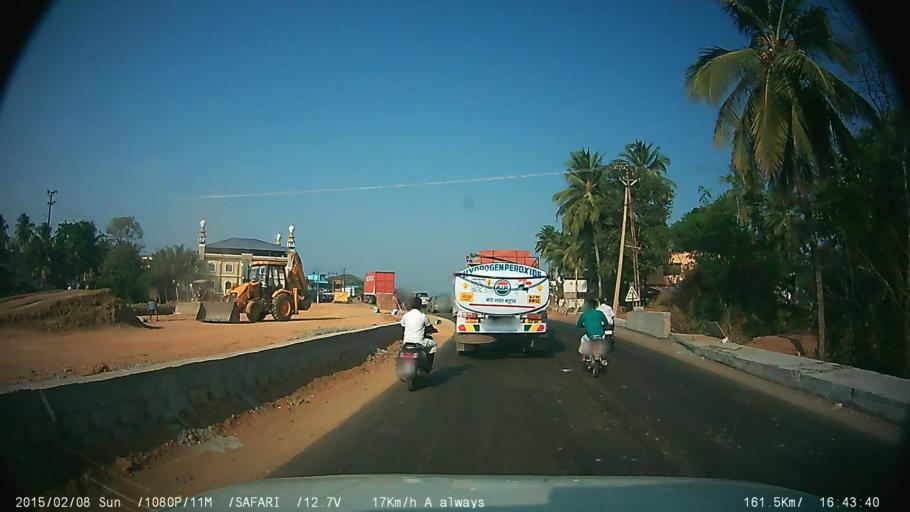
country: IN
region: Kerala
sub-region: Palakkad district
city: Palakkad
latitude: 10.7181
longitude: 76.6000
